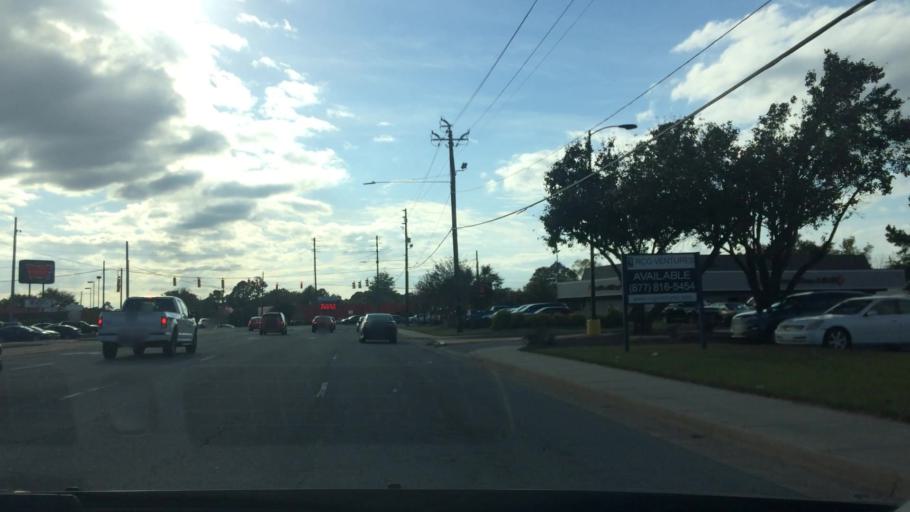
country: US
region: North Carolina
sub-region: Wayne County
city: Goldsboro
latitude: 35.3719
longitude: -77.9519
